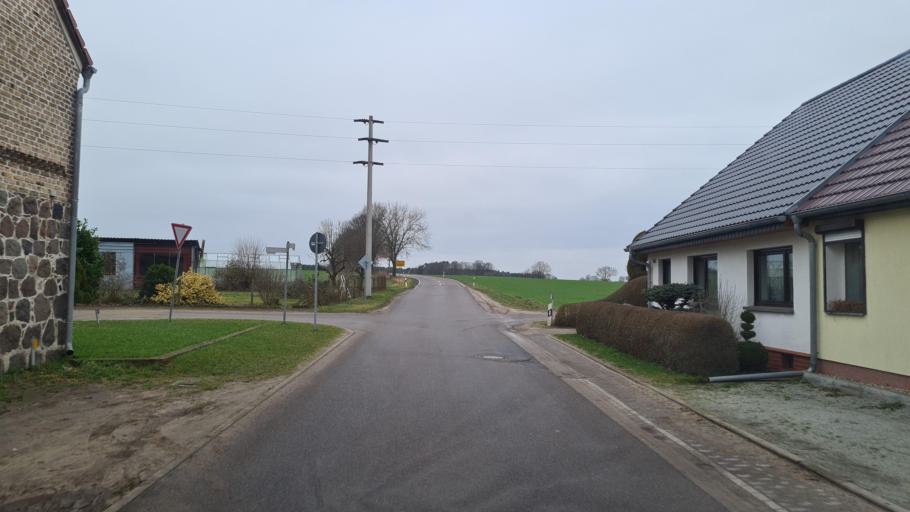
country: DE
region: Brandenburg
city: Zehdenick
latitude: 52.9288
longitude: 13.2540
